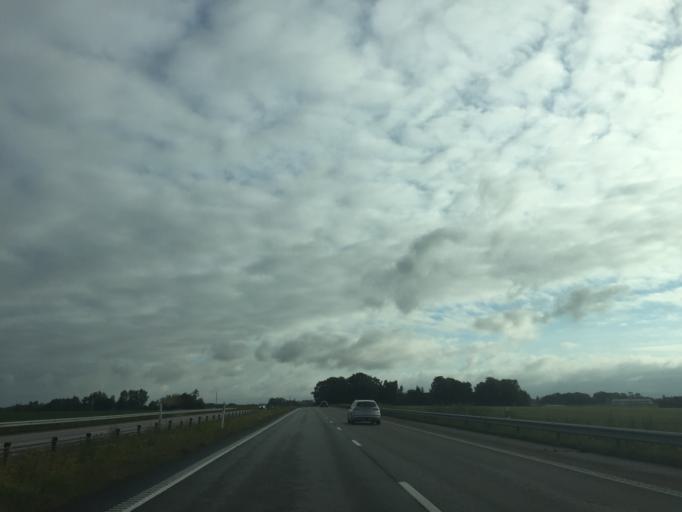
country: SE
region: Skane
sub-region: Angelholms Kommun
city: Strovelstorp
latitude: 56.1370
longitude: 12.8382
